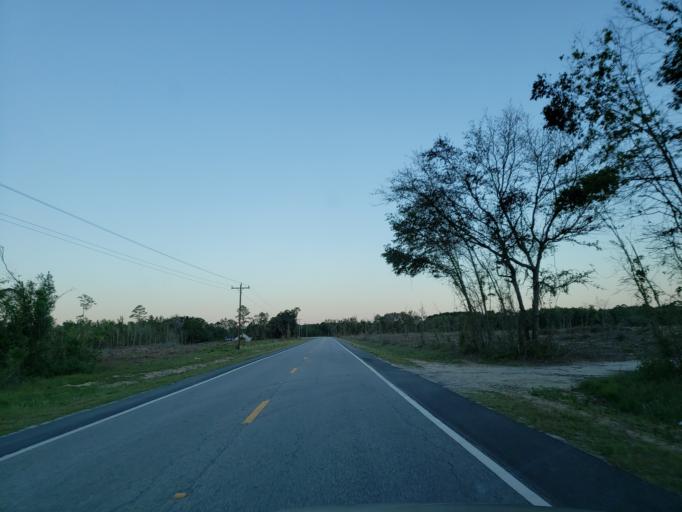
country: US
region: Georgia
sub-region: Echols County
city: Statenville
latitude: 30.5666
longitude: -83.1561
